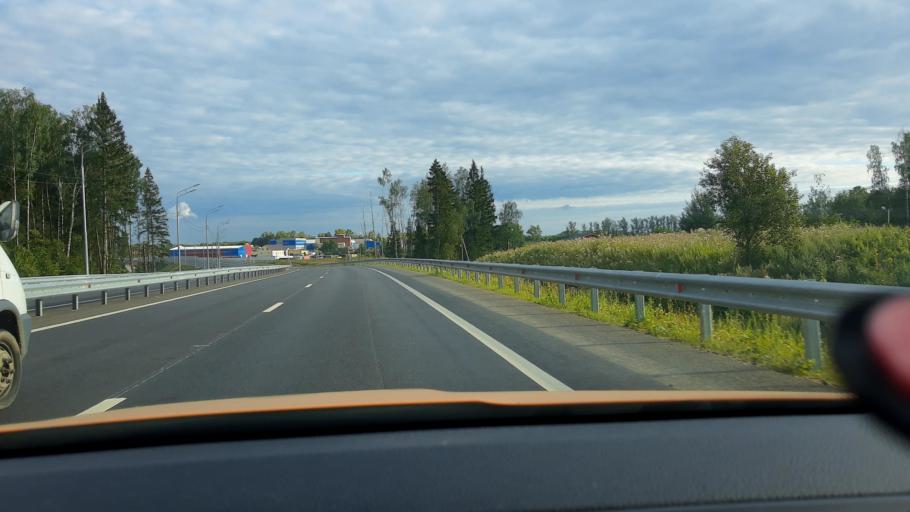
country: RU
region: Moskovskaya
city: Bol'shiye Vyazemy
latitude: 55.6508
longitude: 36.9868
